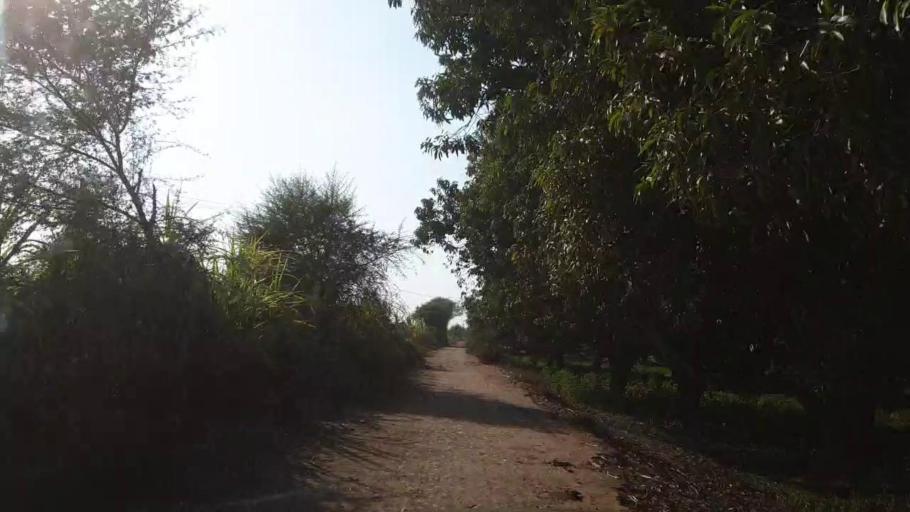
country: PK
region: Sindh
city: Tando Allahyar
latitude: 25.5704
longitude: 68.6460
